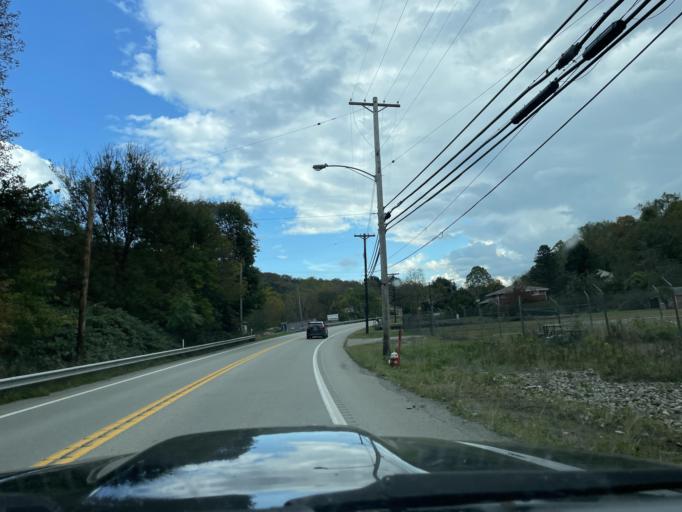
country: US
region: Pennsylvania
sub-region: Westmoreland County
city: Lower Burrell
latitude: 40.5420
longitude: -79.7244
